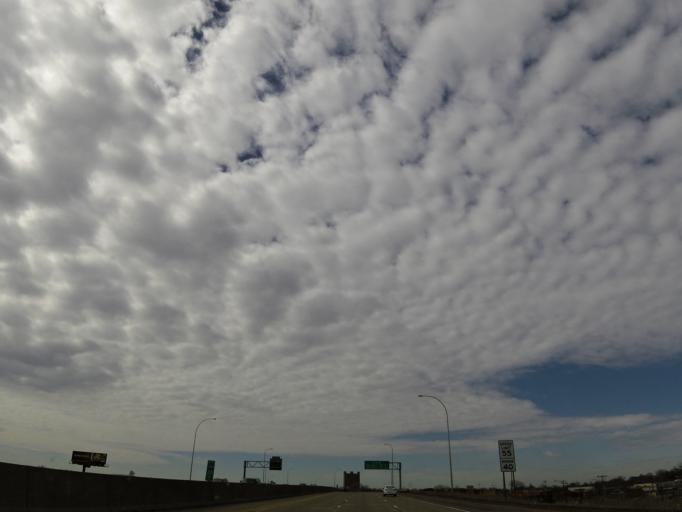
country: US
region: Minnesota
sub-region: Hennepin County
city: Saint Anthony
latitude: 45.0015
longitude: -93.2273
